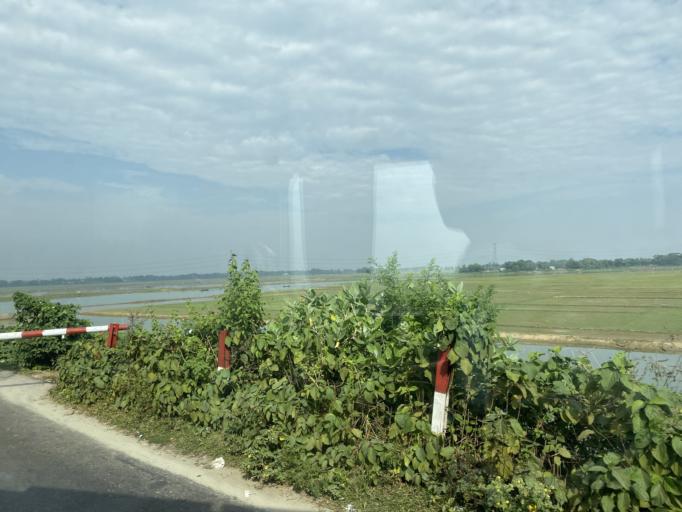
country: IN
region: Tripura
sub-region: West Tripura
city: Agartala
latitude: 23.8797
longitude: 91.2027
